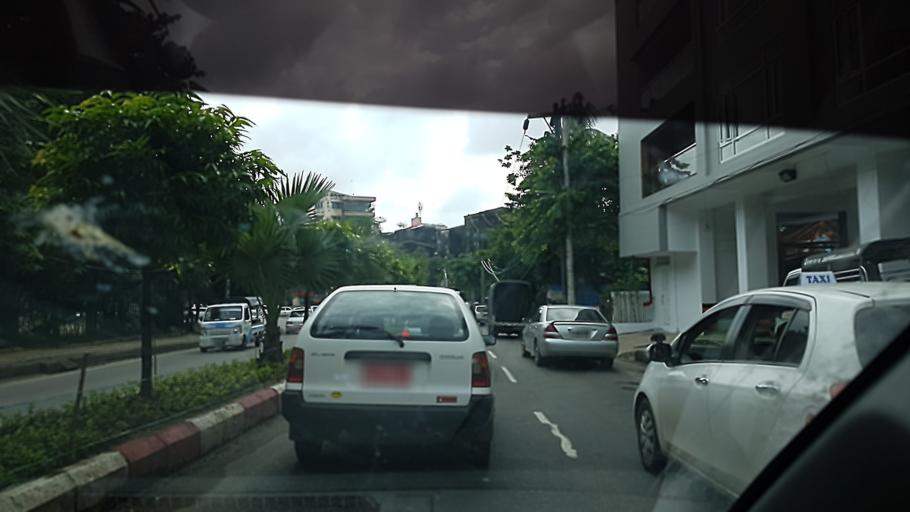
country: MM
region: Yangon
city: Yangon
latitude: 16.7944
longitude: 96.1714
